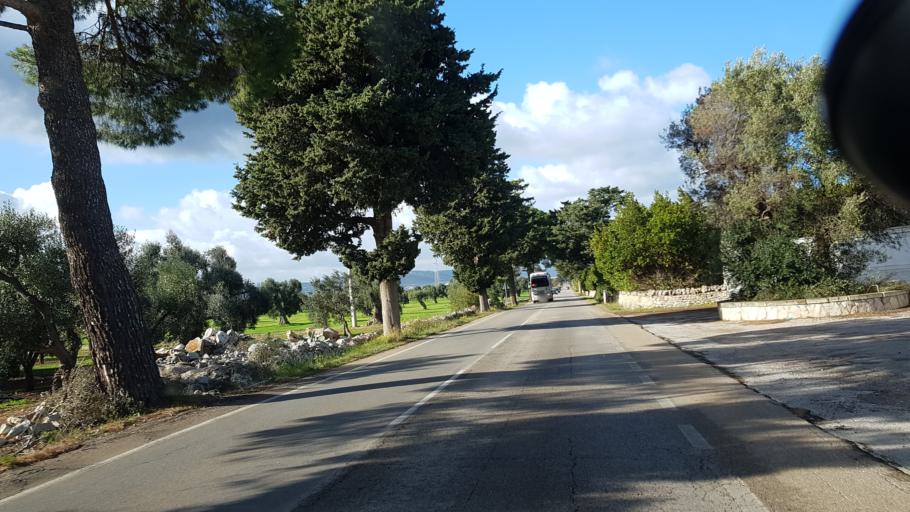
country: IT
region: Apulia
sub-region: Provincia di Brindisi
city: Pezze di Greco
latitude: 40.8015
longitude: 17.4381
